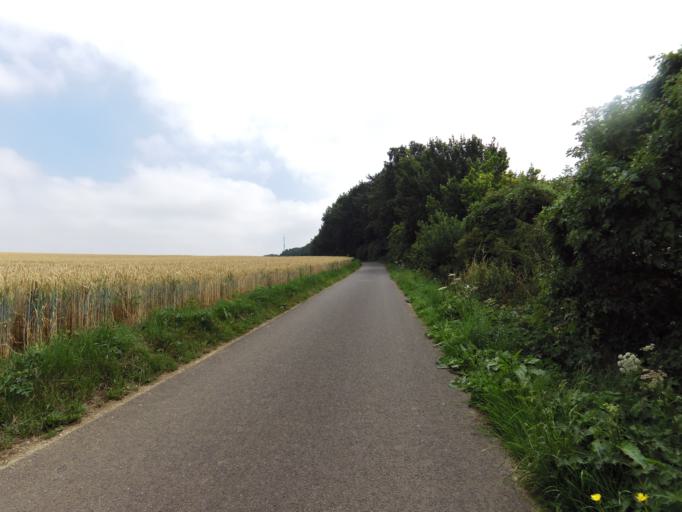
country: NL
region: Limburg
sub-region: Gemeente Voerendaal
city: Ubachsberg
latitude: 50.8313
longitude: 5.9116
